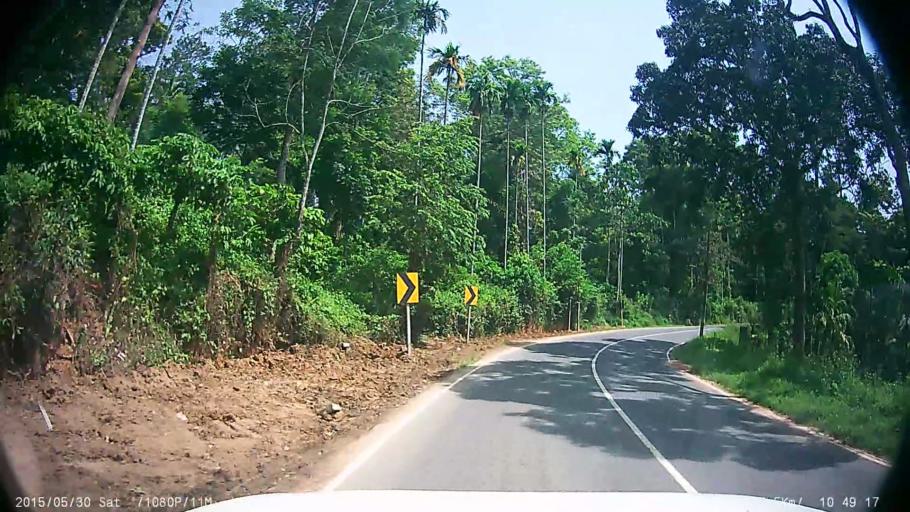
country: IN
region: Kerala
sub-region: Wayanad
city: Kalpetta
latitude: 11.6363
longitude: 76.0864
